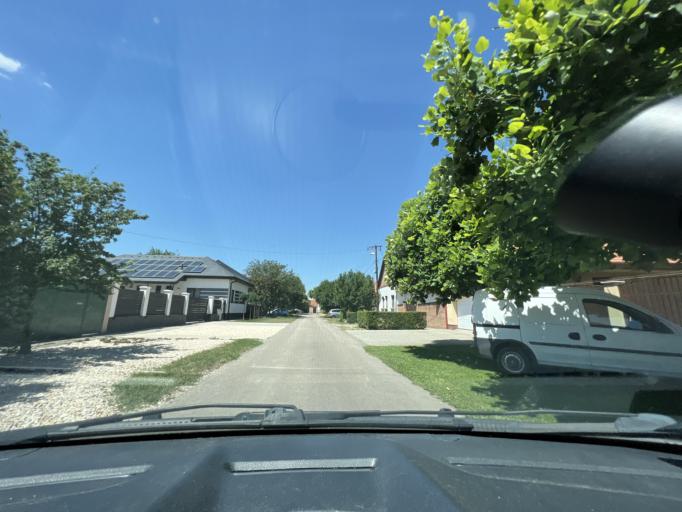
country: HU
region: Csongrad
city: Szeged
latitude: 46.2461
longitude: 20.1289
